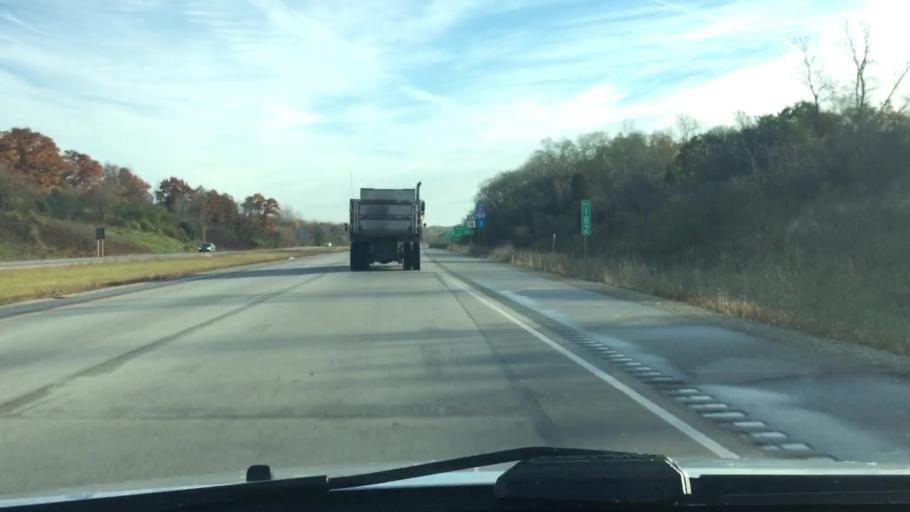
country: US
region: Wisconsin
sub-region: Waukesha County
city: Hartland
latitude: 43.1074
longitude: -88.3565
